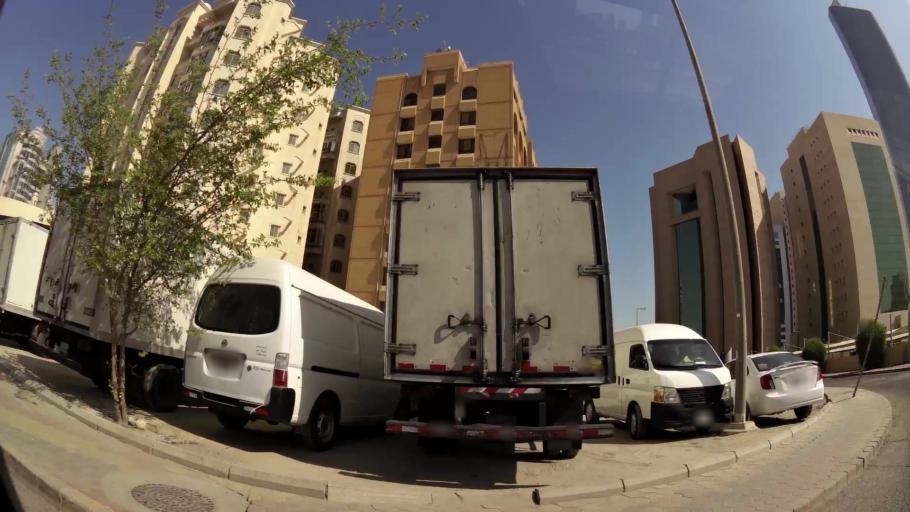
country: KW
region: Al Asimah
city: Kuwait City
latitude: 29.3809
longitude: 47.9885
